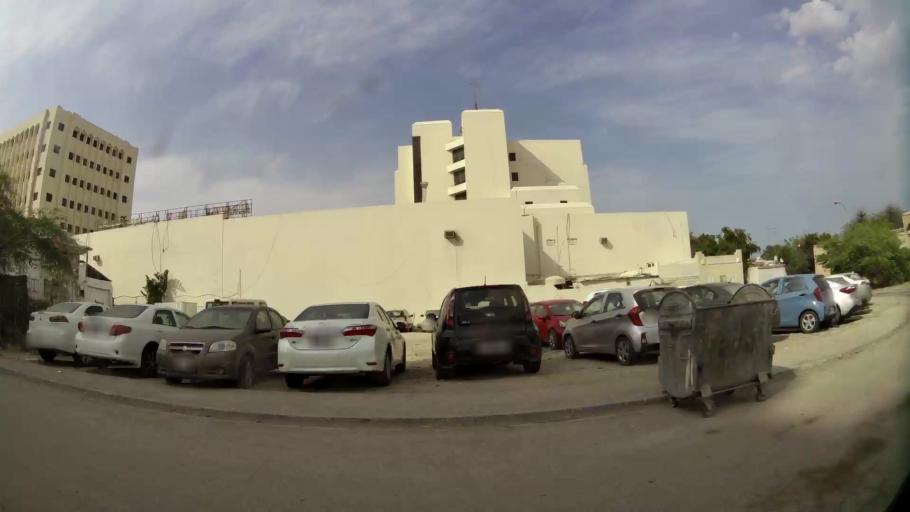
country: QA
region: Baladiyat ad Dawhah
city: Doha
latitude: 25.2879
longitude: 51.5220
